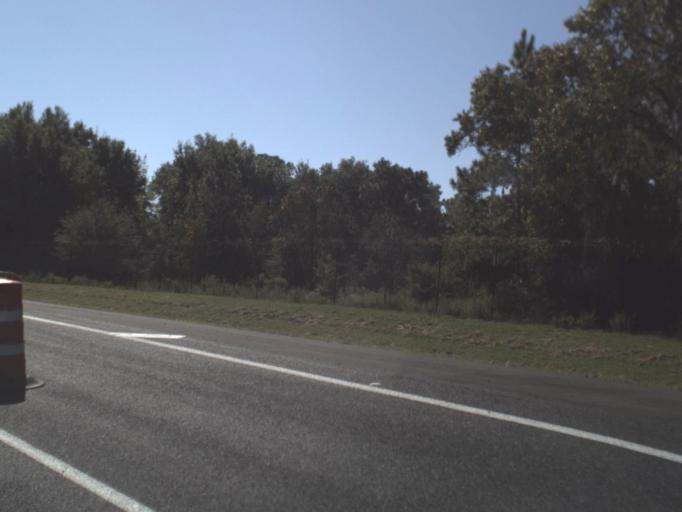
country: US
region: Florida
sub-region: Citrus County
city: Sugarmill Woods
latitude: 28.6478
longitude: -82.4928
